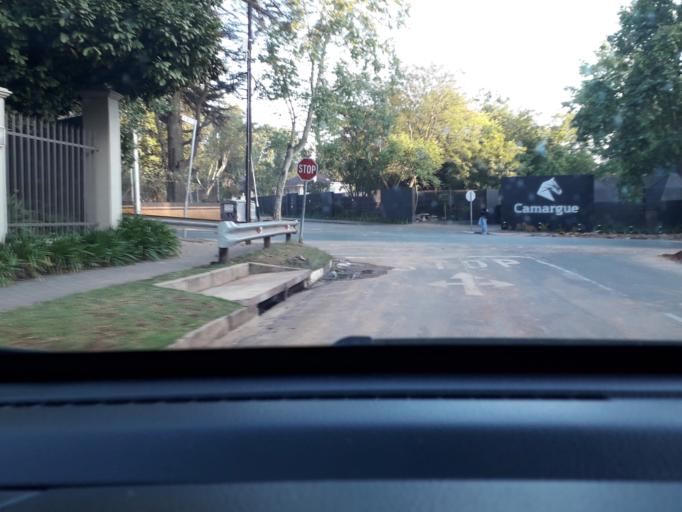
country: ZA
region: Gauteng
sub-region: City of Johannesburg Metropolitan Municipality
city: Johannesburg
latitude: -26.1479
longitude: 28.0517
